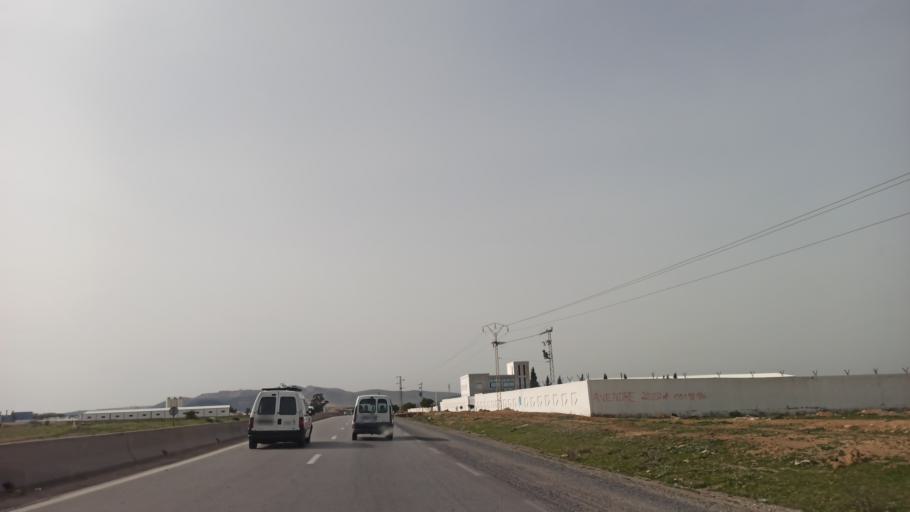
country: TN
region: Tunis
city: La Mohammedia
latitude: 36.5711
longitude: 10.0866
